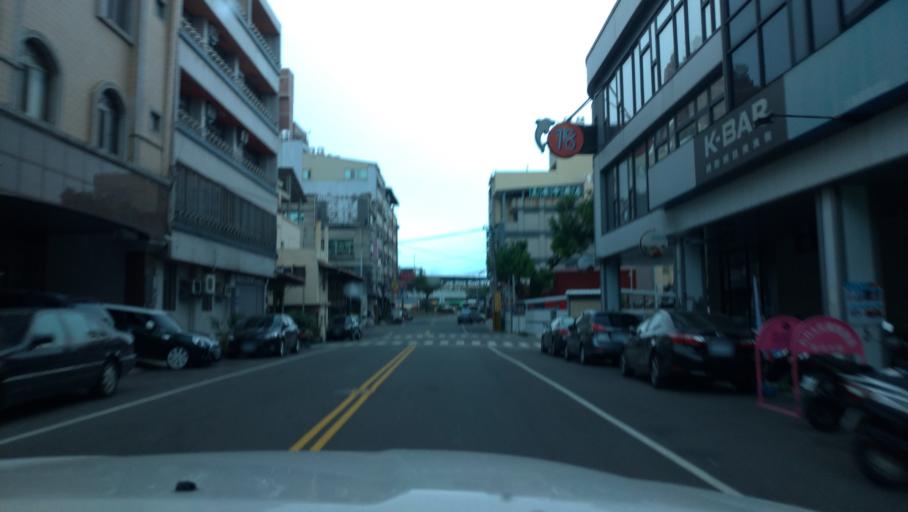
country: TW
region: Taiwan
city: Fengyuan
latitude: 24.2529
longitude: 120.7255
